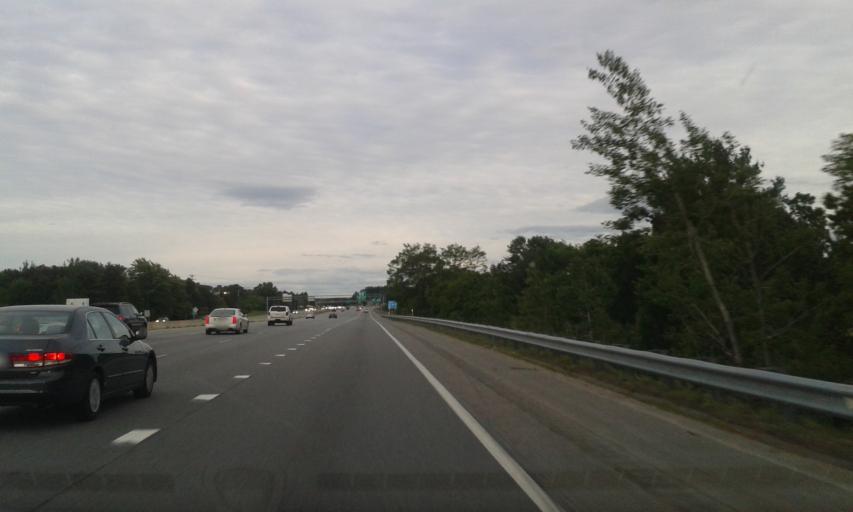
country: US
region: New Hampshire
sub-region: Hillsborough County
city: Nashua
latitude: 42.7587
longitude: -71.4936
